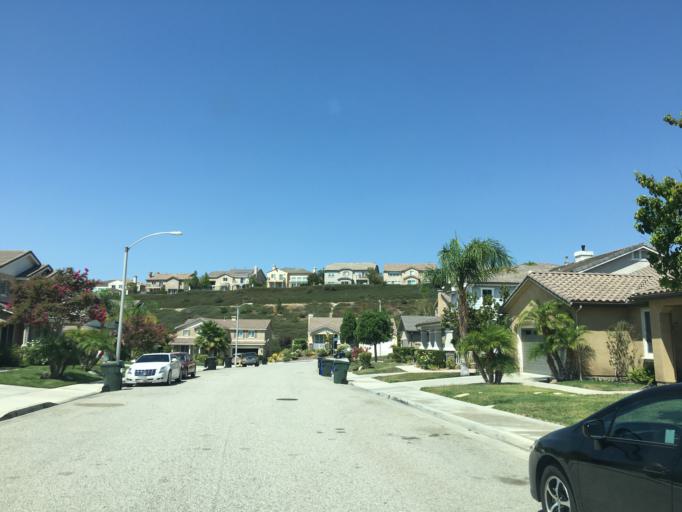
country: US
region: California
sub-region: Los Angeles County
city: Valencia
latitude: 34.4709
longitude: -118.5603
